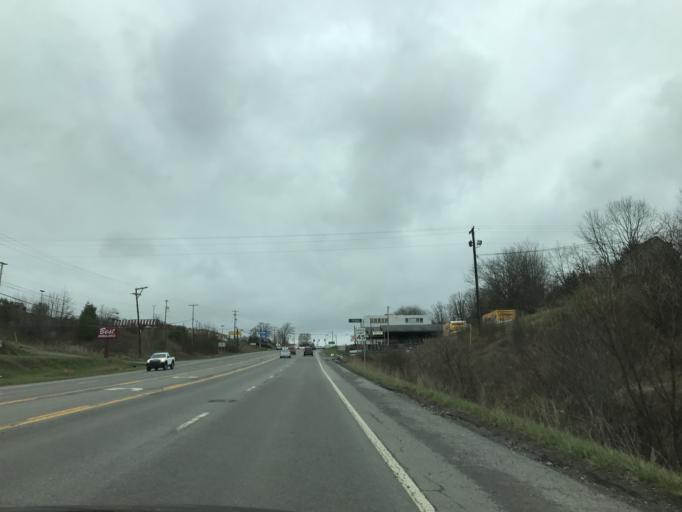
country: US
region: West Virginia
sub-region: Raleigh County
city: MacArthur
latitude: 37.7508
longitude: -81.2206
